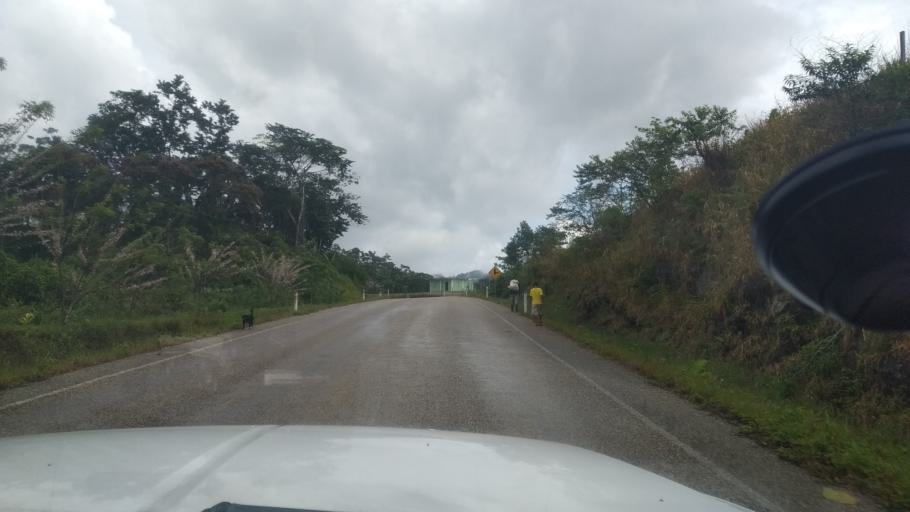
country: GT
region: Peten
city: San Luis
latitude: 16.1990
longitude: -89.1522
